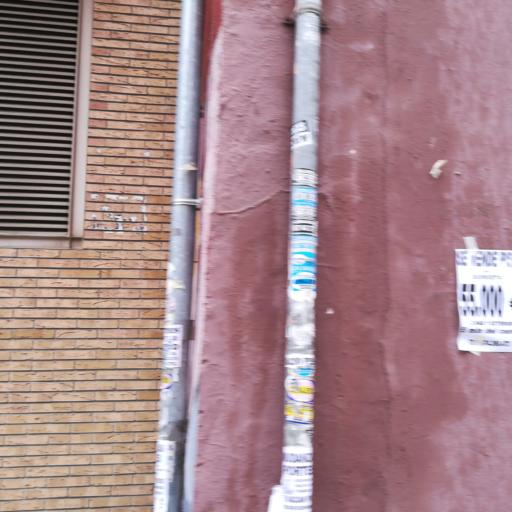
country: ES
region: Valencia
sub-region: Provincia de Valencia
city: Valencia
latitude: 39.4555
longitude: -0.3843
